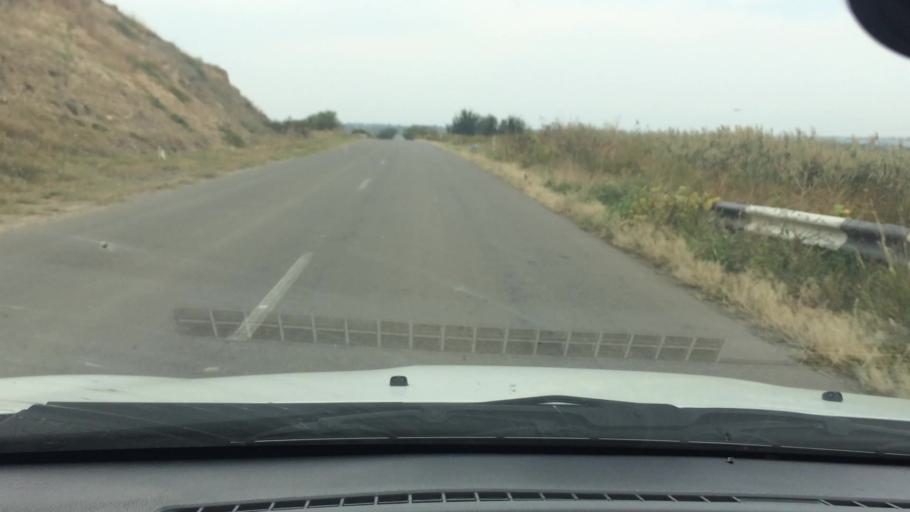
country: AM
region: Tavush
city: Berdavan
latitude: 41.3406
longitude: 44.9950
